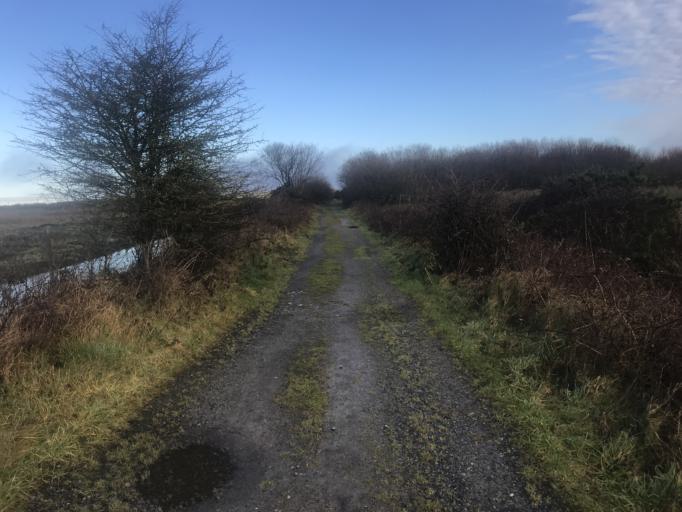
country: IE
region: Connaught
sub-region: County Galway
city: Gaillimh
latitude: 53.3209
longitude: -9.0151
